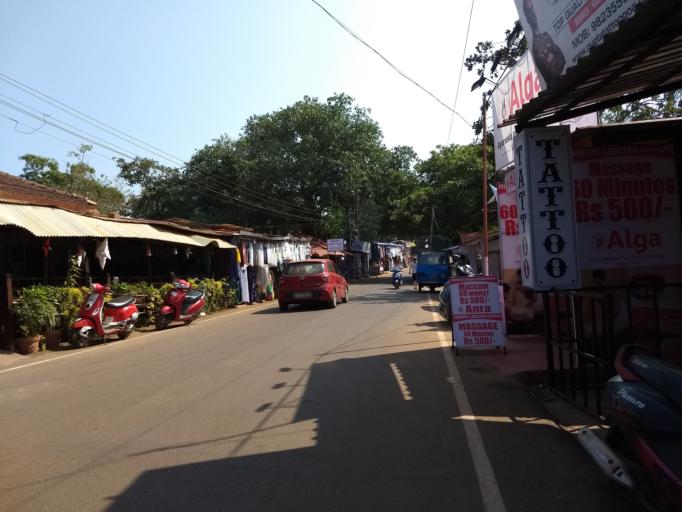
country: IN
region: Goa
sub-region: North Goa
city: Vagator
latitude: 15.6002
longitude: 73.7362
